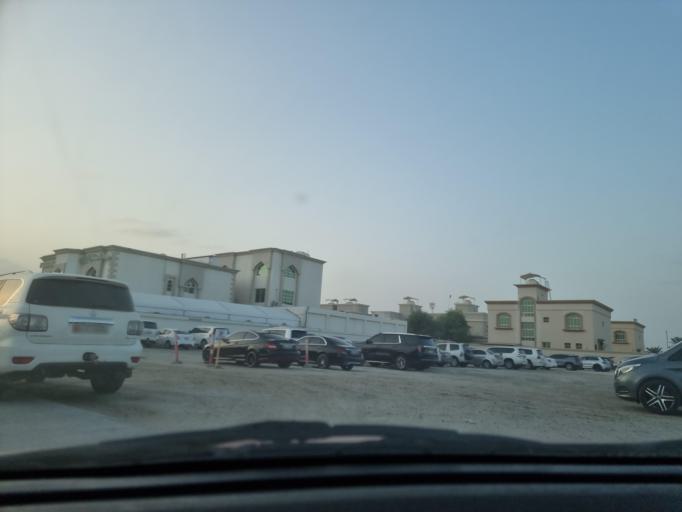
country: AE
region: Abu Dhabi
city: Abu Dhabi
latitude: 24.4066
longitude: 54.6026
